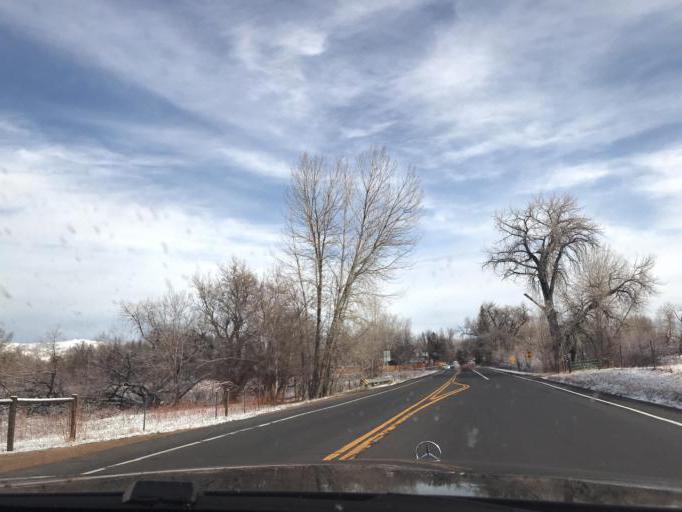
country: US
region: Colorado
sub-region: Boulder County
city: Boulder
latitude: 39.9983
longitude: -105.2127
